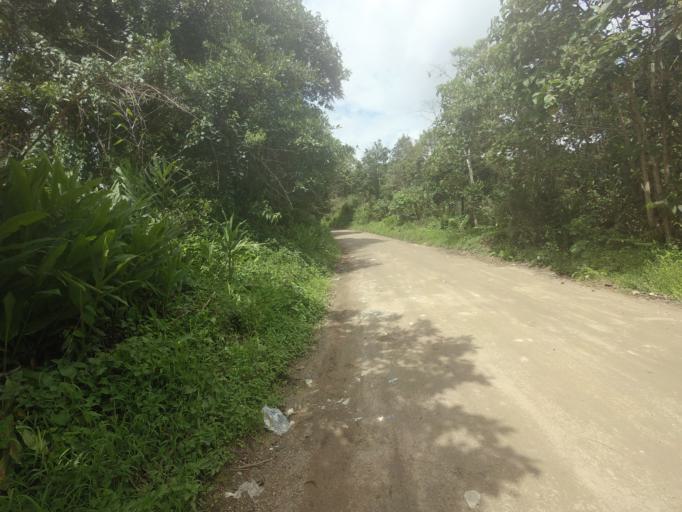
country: CO
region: Huila
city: San Agustin
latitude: 1.8891
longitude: -76.2965
